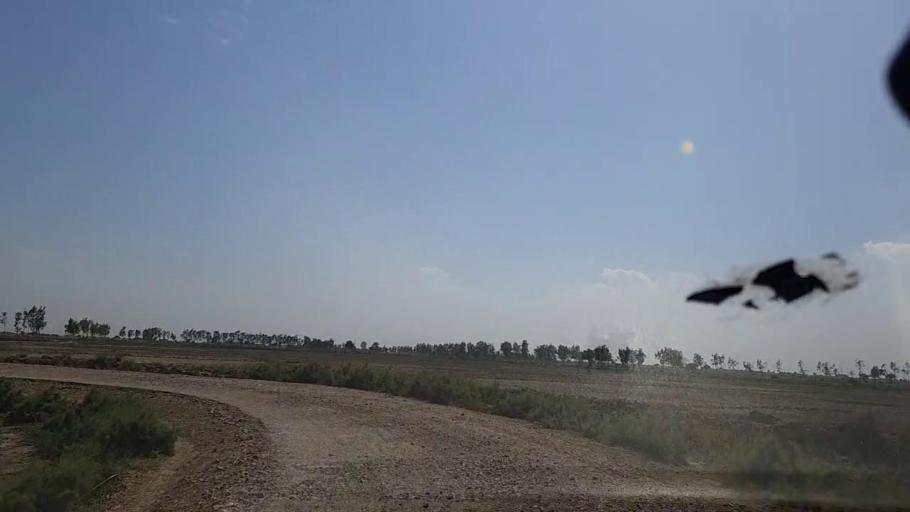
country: PK
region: Sindh
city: Daro Mehar
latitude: 24.6636
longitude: 68.0809
